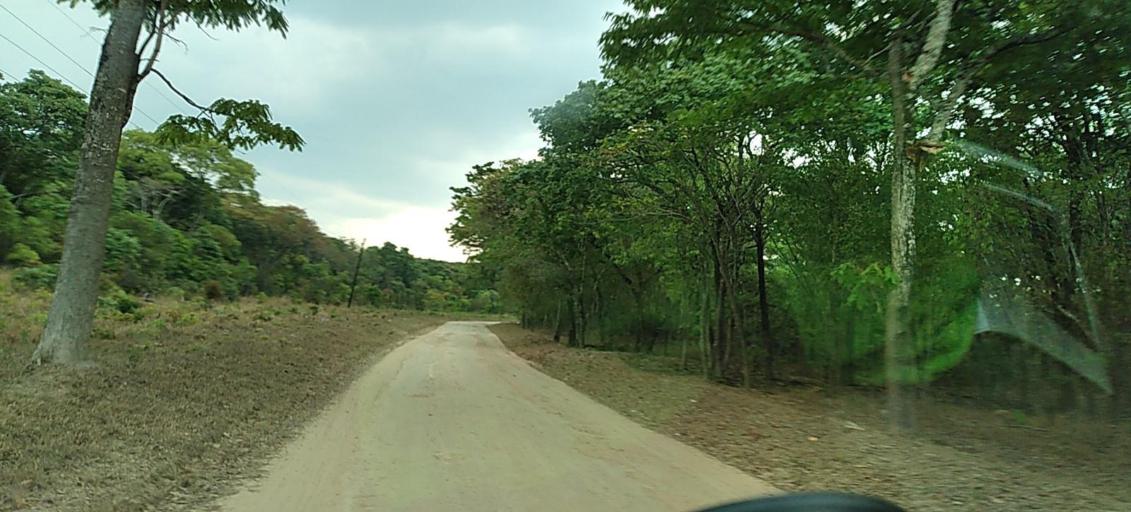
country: ZM
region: North-Western
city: Solwezi
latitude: -12.7740
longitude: 26.4695
